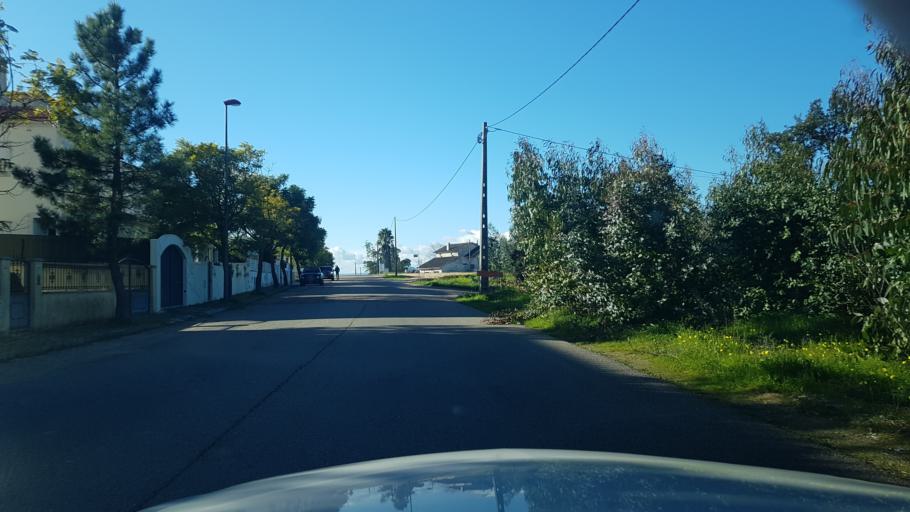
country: PT
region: Santarem
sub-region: Entroncamento
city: Entroncamento
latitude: 39.4769
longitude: -8.4941
